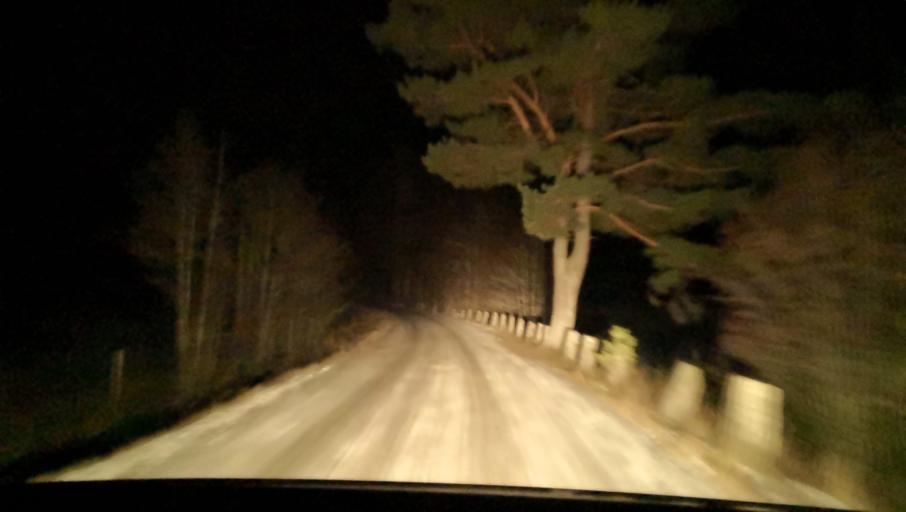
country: SE
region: Stockholm
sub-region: Nacka Kommun
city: Fisksatra
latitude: 59.2894
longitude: 18.2229
